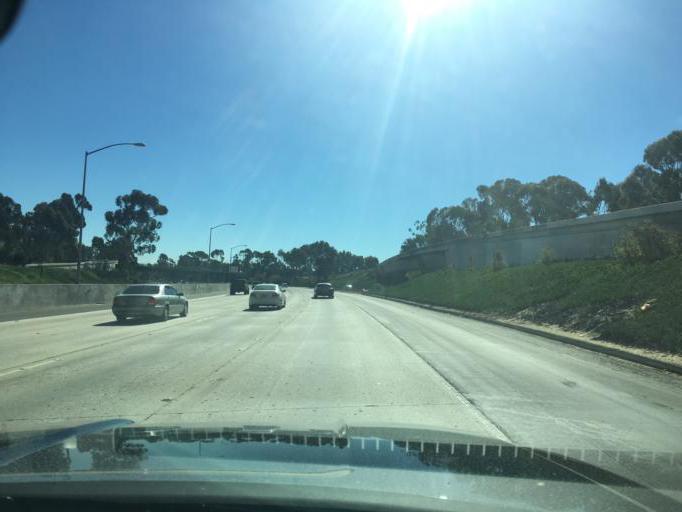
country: US
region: California
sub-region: San Diego County
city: National City
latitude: 32.7155
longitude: -117.1030
